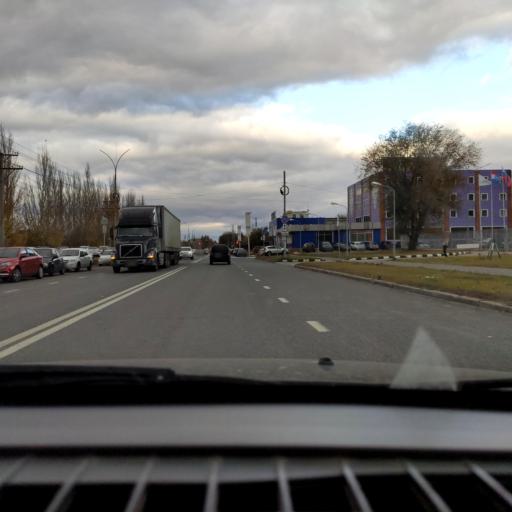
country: RU
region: Samara
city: Tol'yatti
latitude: 53.5581
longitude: 49.2945
